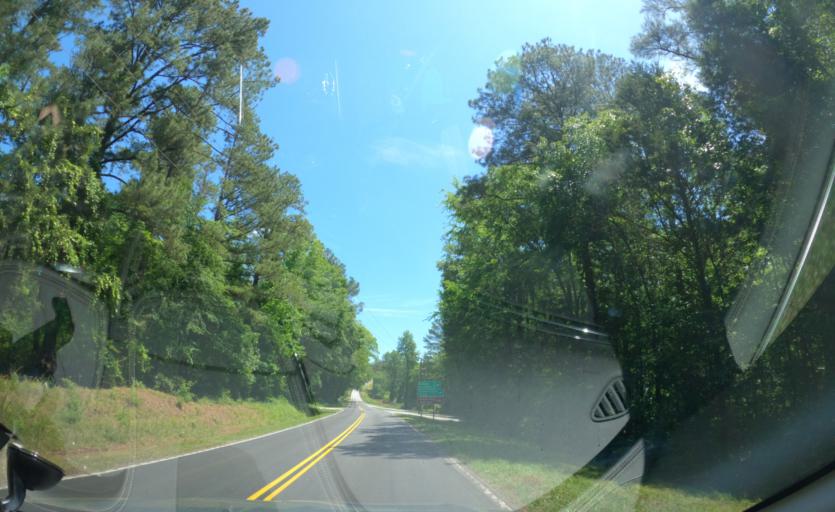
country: US
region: South Carolina
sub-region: McCormick County
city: McCormick
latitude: 33.9495
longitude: -82.4326
